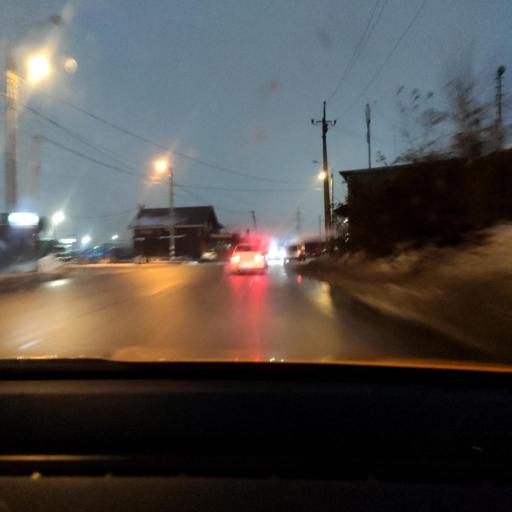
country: RU
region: Moskovskaya
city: Mosrentgen
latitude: 55.6209
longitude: 37.4485
